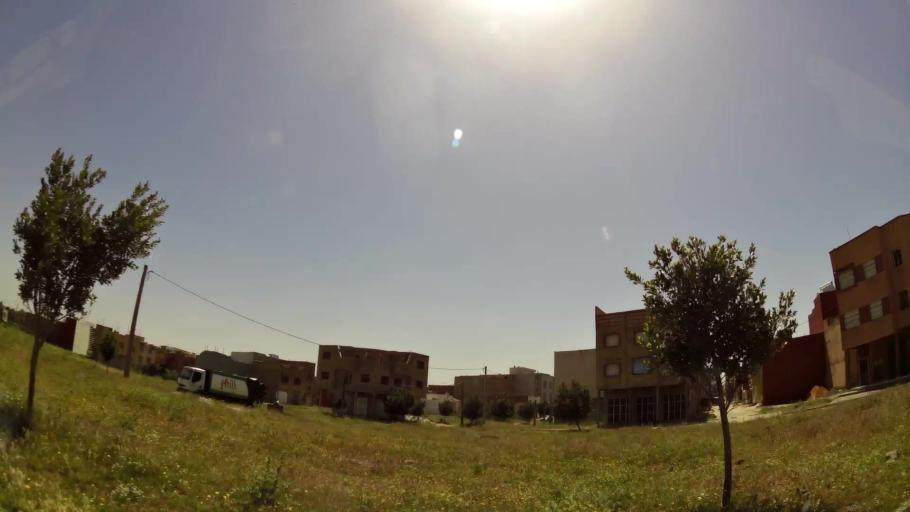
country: MA
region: Rabat-Sale-Zemmour-Zaer
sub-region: Khemisset
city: Khemisset
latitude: 33.8084
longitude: -6.0884
